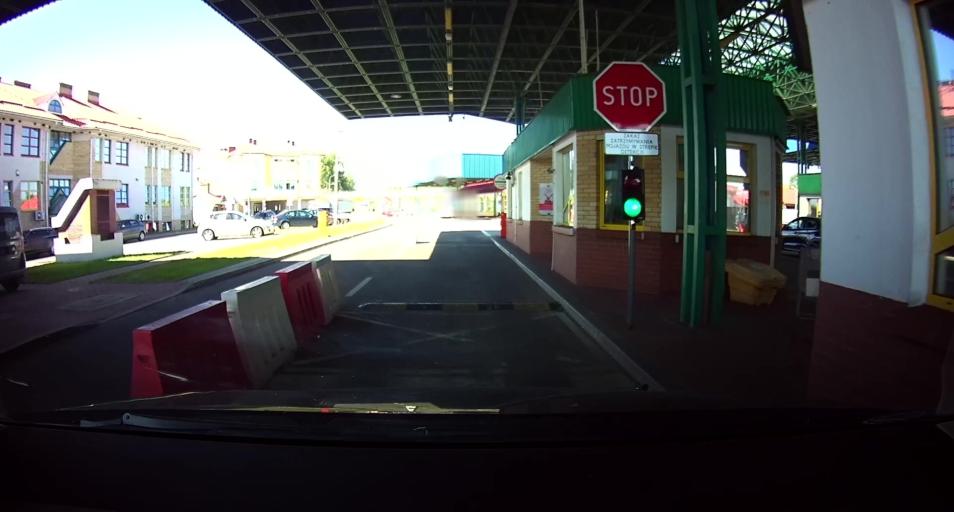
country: BY
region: Grodnenskaya
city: Vyalikaya Byerastavitsa
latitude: 53.1239
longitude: 23.8909
